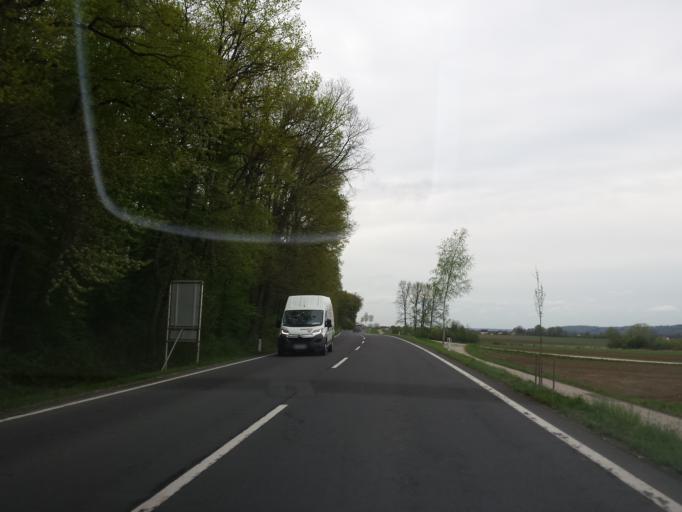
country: AT
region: Burgenland
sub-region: Politischer Bezirk Jennersdorf
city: Konigsdorf
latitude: 47.0179
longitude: 16.1616
